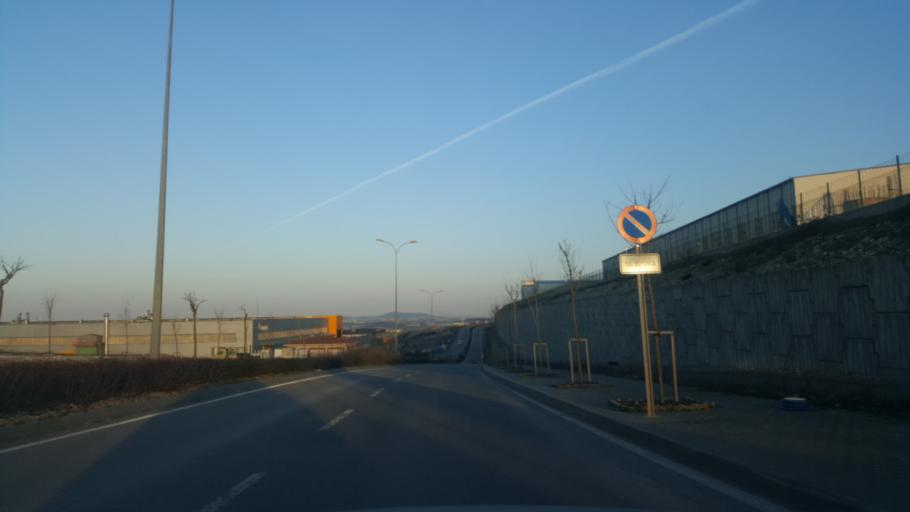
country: TR
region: Kocaeli
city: Tavsanli
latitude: 40.8312
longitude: 29.5573
